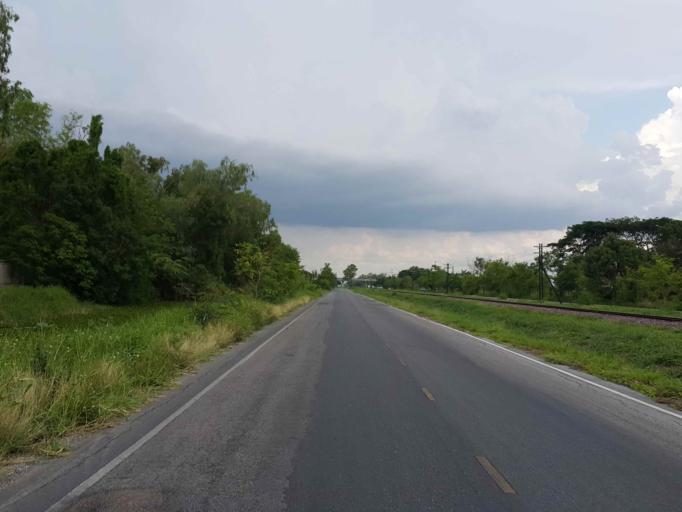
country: TH
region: Chiang Mai
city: Saraphi
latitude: 18.7397
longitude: 99.0292
